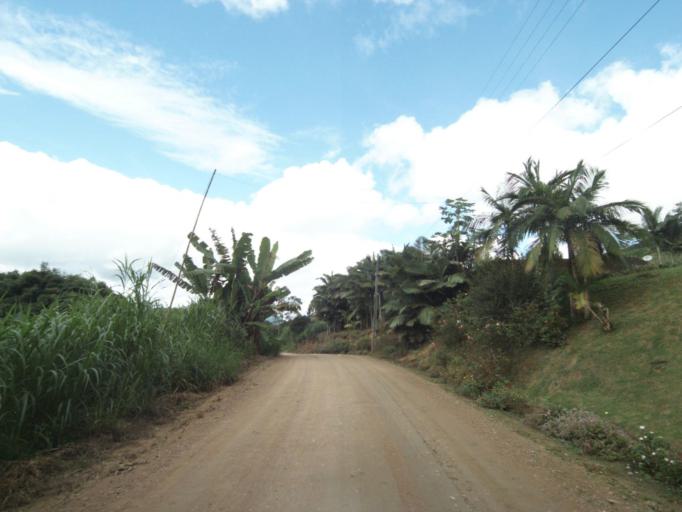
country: BR
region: Santa Catarina
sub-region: Pomerode
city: Pomerode
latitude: -26.6707
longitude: -49.1897
